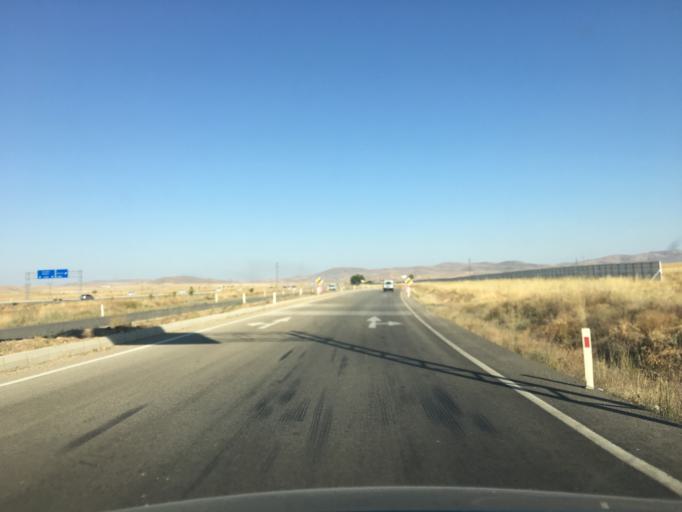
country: TR
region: Kirsehir
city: Akpinar
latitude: 39.3283
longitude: 34.0354
